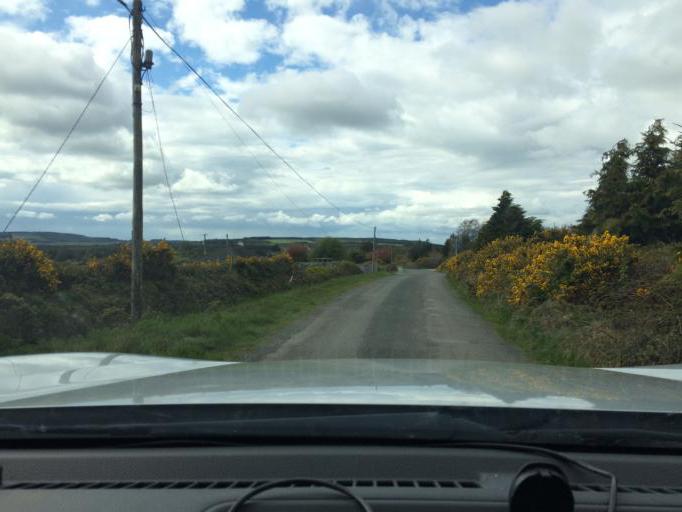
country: IE
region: Munster
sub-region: Waterford
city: Dungarvan
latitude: 52.0419
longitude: -7.6463
